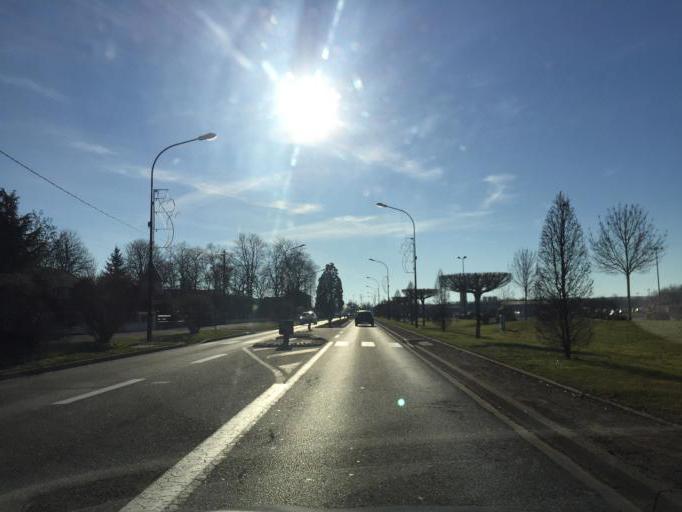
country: FR
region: Auvergne
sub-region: Departement de l'Allier
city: Saint-Remy-en-Rollat
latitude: 46.1598
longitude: 3.3929
